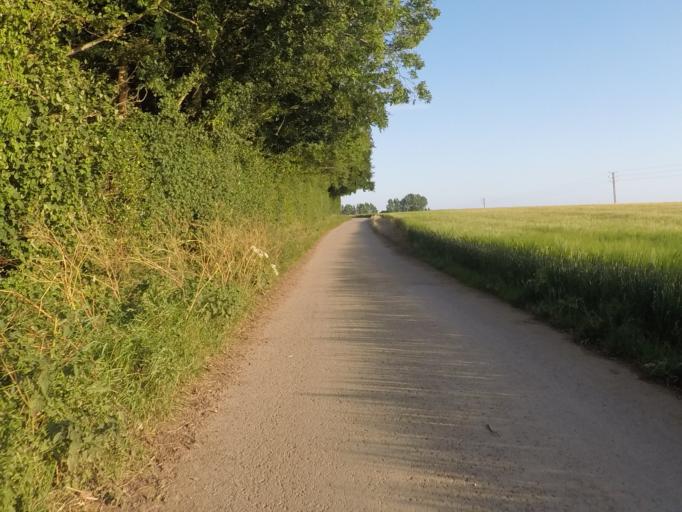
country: GB
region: England
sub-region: Oxfordshire
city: Charlbury
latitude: 51.8817
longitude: -1.4493
